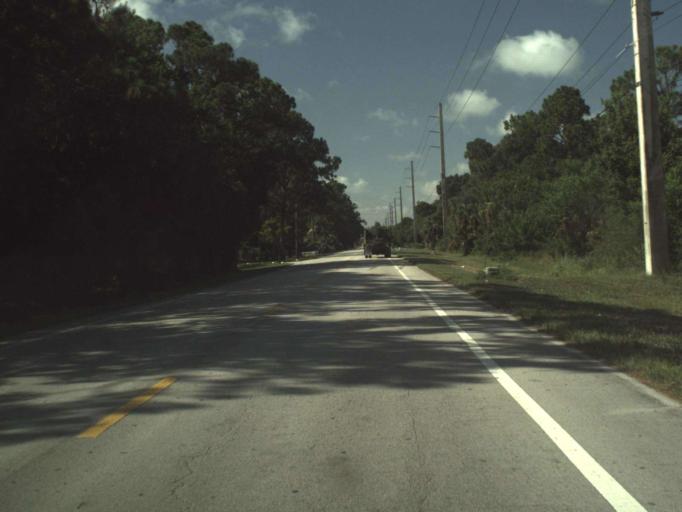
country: US
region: Florida
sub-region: Indian River County
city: Gifford
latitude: 27.6585
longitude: -80.4465
